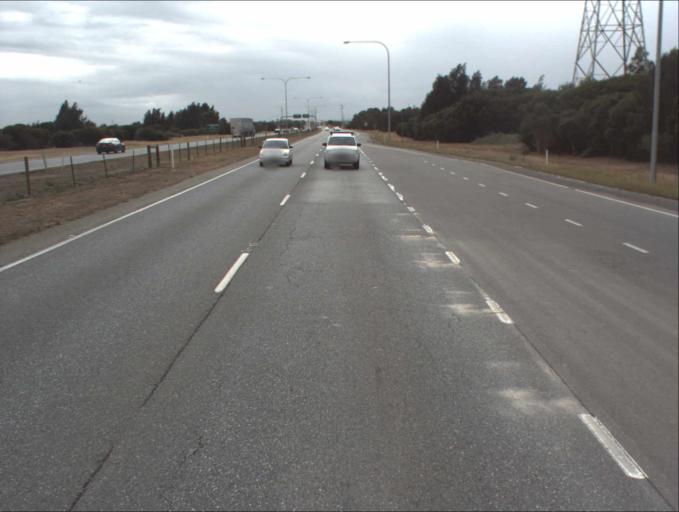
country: AU
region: South Australia
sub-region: Port Adelaide Enfield
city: Enfield
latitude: -34.8183
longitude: 138.5913
